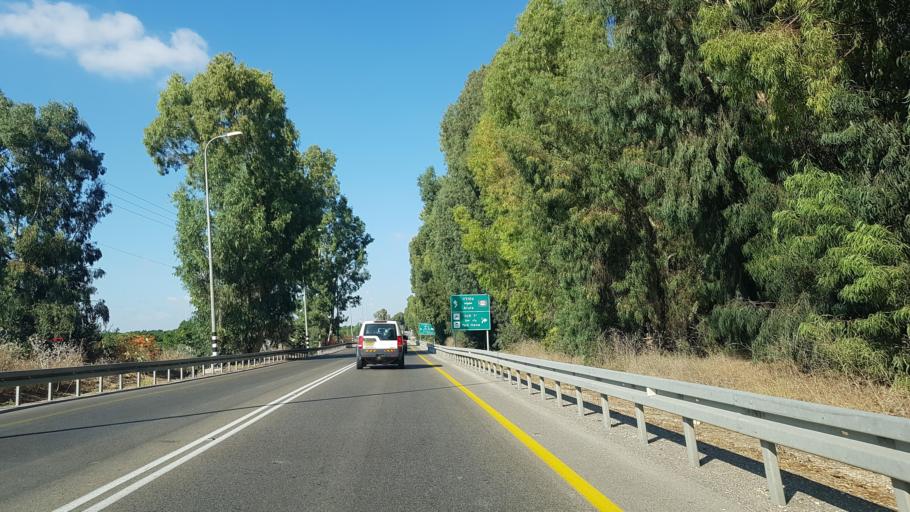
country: PS
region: West Bank
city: Tulkarm
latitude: 32.3221
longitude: 34.9998
